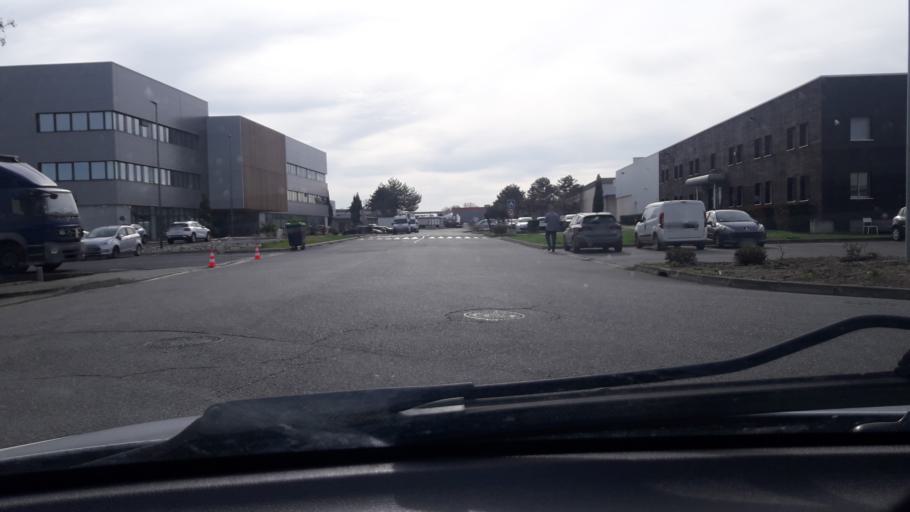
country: FR
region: Midi-Pyrenees
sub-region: Departement de la Haute-Garonne
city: Portet-sur-Garonne
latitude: 43.5560
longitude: 1.4166
